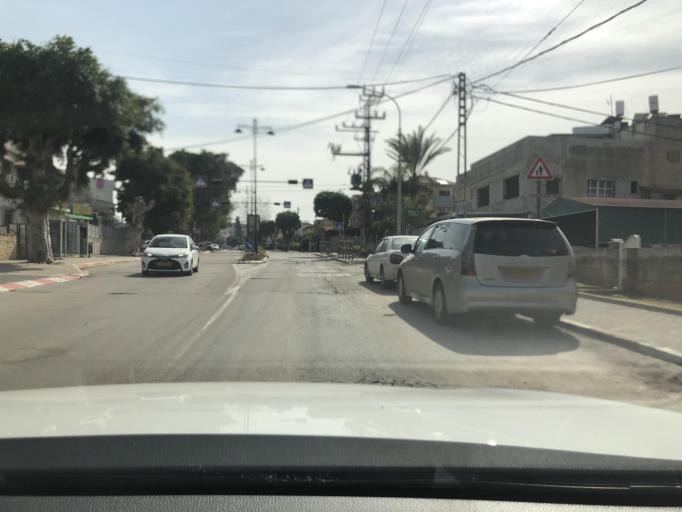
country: IL
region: Central District
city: Rosh Ha'Ayin
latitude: 32.0905
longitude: 34.9485
